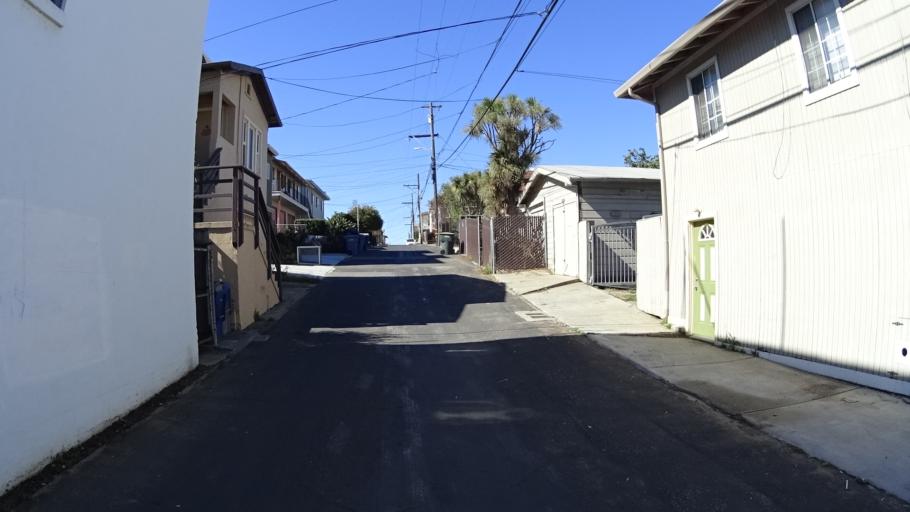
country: US
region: California
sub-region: San Mateo County
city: South San Francisco
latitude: 37.6579
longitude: -122.4198
